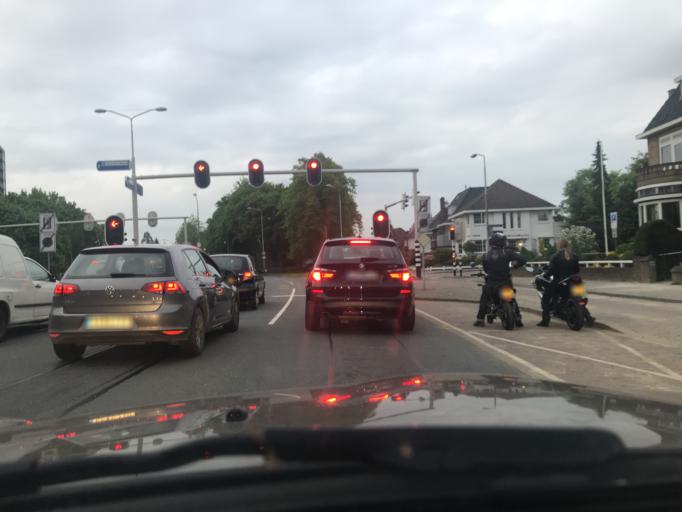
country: NL
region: Limburg
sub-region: Gemeente Venlo
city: Venlo
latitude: 51.3697
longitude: 6.1778
